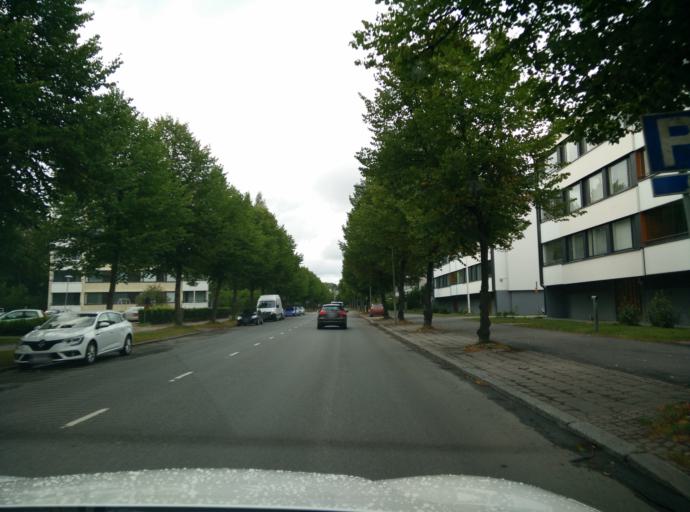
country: FI
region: Haeme
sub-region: Haemeenlinna
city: Haemeenlinna
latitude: 60.9972
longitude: 24.4400
